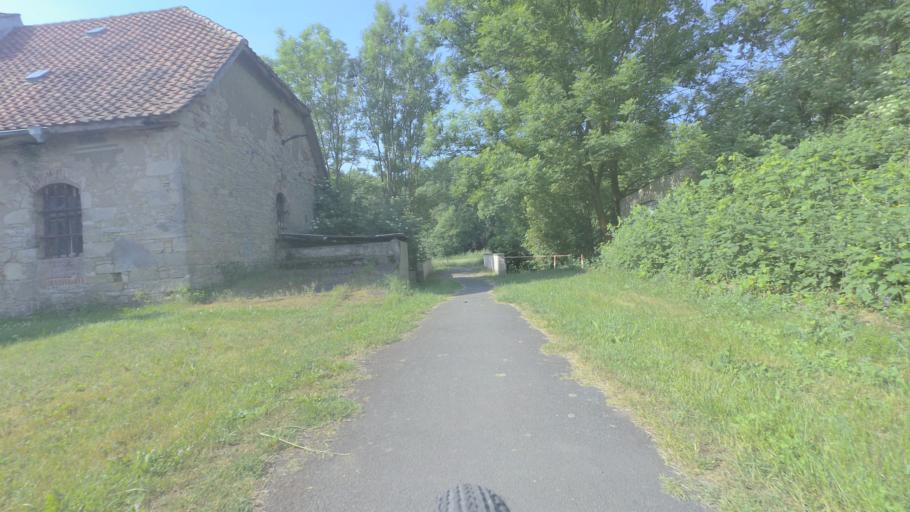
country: DE
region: Saxony-Anhalt
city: Nachterstedt
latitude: 51.7661
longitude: 11.3460
